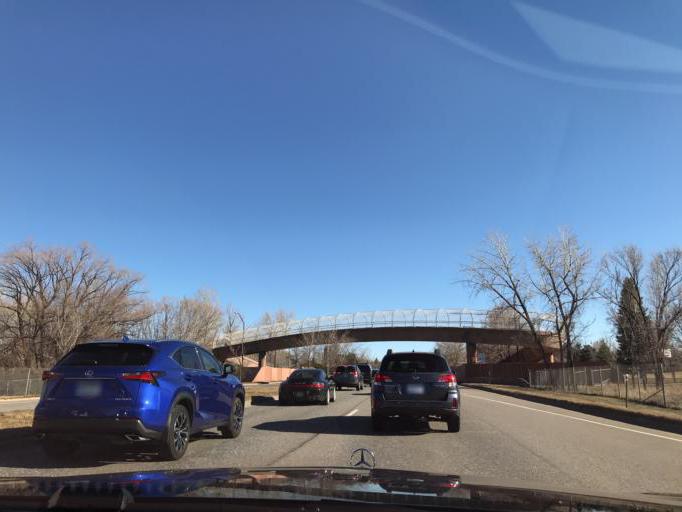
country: US
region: Colorado
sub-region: Boulder County
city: Boulder
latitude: 40.0077
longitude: -105.2392
